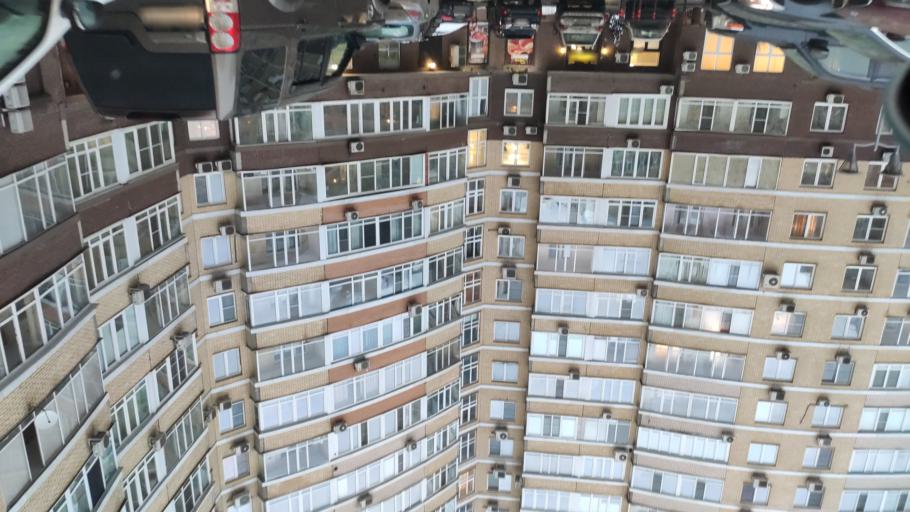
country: RU
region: Moscow
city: Nikulino
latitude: 55.6660
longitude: 37.4714
